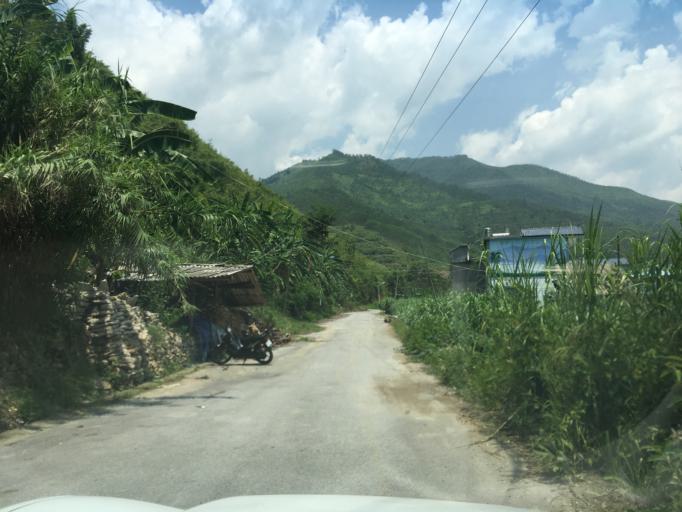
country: CN
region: Guangxi Zhuangzu Zizhiqu
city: Xinzhou
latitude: 24.9074
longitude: 105.4741
